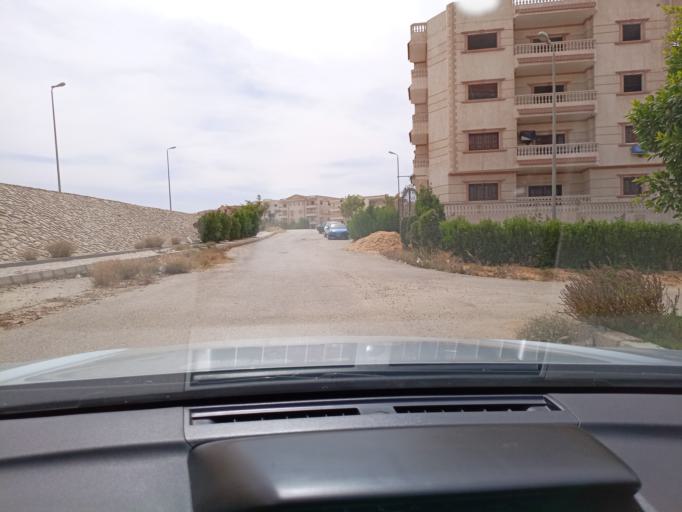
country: EG
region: Muhafazat al Qalyubiyah
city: Al Khankah
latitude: 30.2432
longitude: 31.4911
